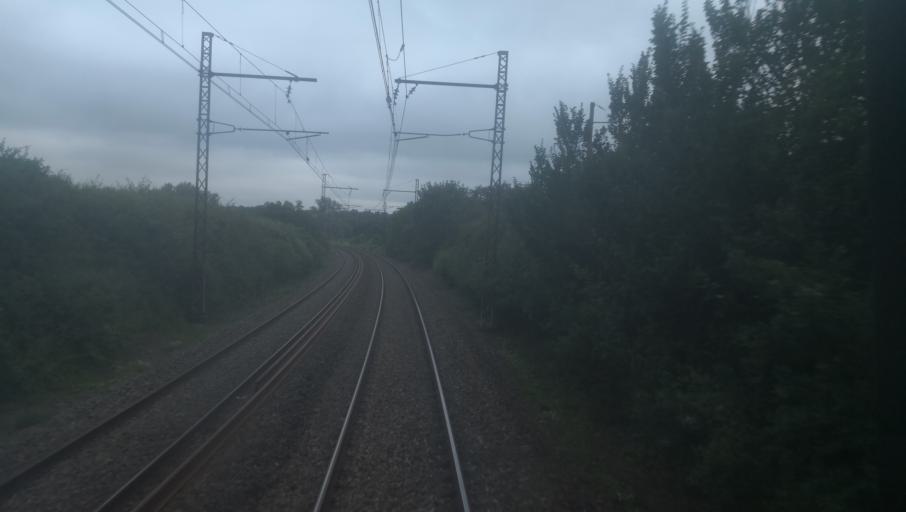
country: FR
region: Centre
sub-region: Departement de l'Indre
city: Sainte-Lizaigne
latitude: 47.0257
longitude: 2.0420
